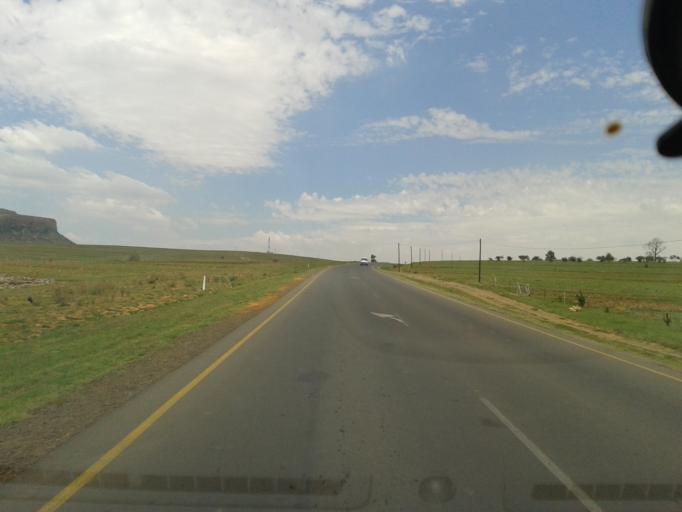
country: LS
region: Maseru
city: Maseru
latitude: -29.3678
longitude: 27.6448
